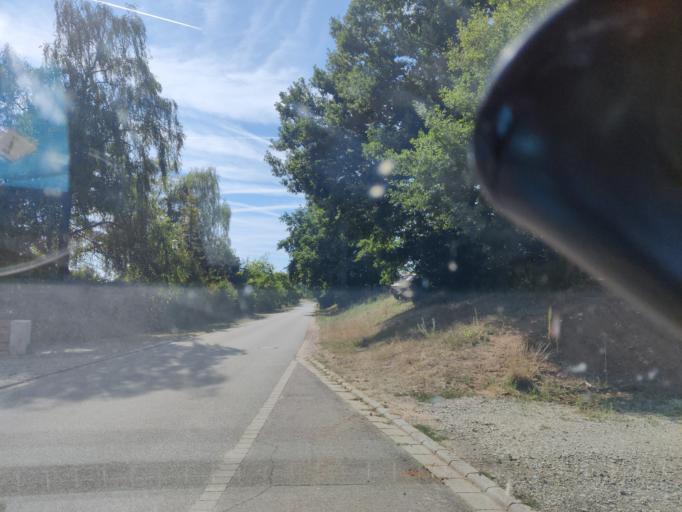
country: DE
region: Bavaria
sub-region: Regierungsbezirk Mittelfranken
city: Hilpoltstein
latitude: 49.1985
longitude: 11.2124
